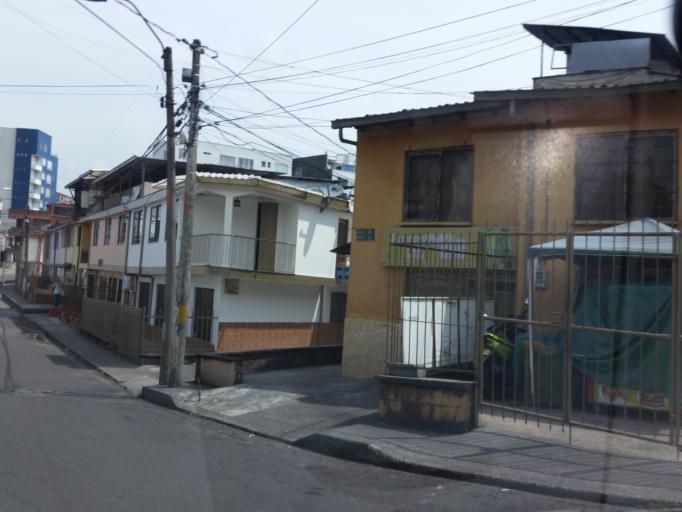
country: CO
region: Caldas
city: Manizales
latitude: 5.0761
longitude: -75.5253
